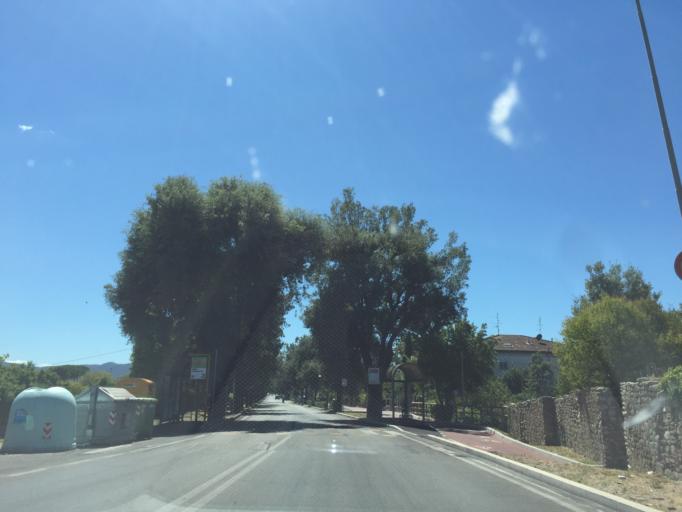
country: IT
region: Tuscany
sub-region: Provincia di Pistoia
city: Pistoia
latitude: 43.9377
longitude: 10.9248
